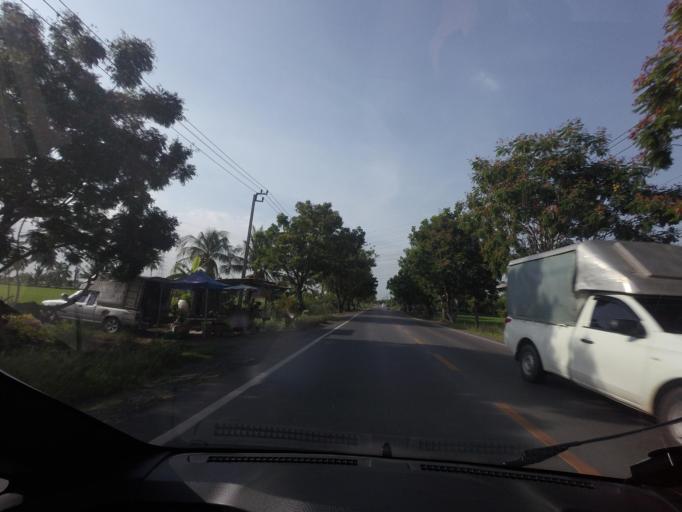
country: TH
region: Bangkok
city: Lat Krabang
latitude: 13.7260
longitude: 100.8574
